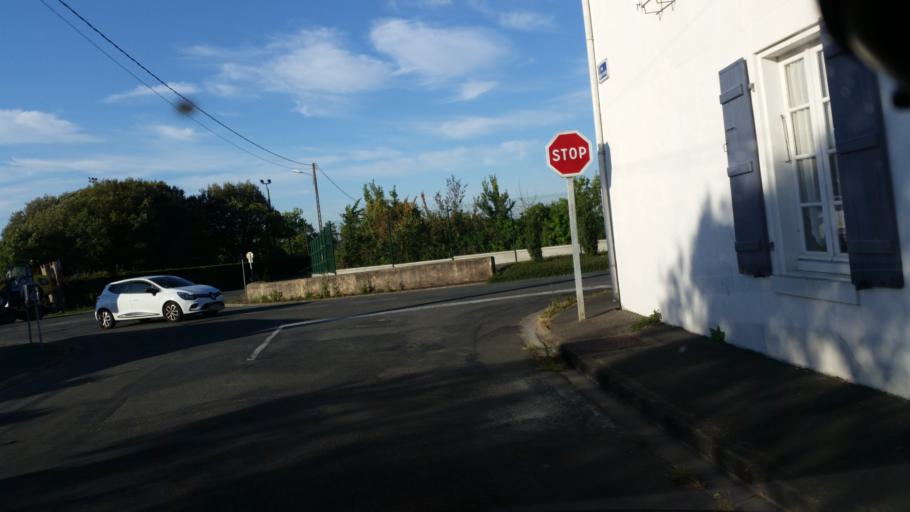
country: FR
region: Poitou-Charentes
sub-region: Departement de la Charente-Maritime
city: Marans
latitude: 46.3038
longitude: -0.9939
